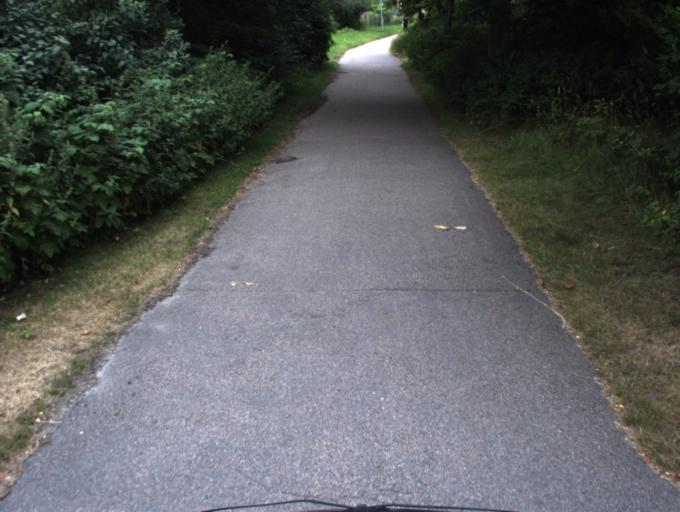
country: SE
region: Skane
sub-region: Helsingborg
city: Helsingborg
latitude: 56.0688
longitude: 12.6993
